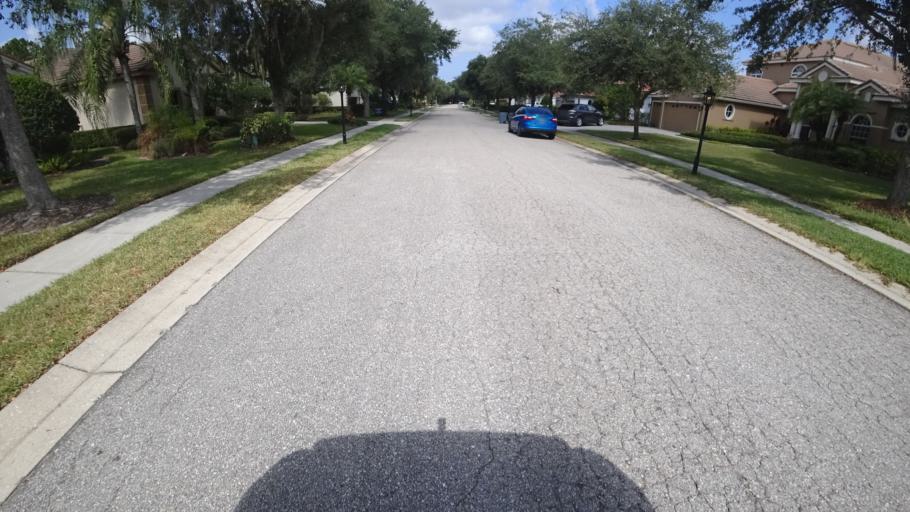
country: US
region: Florida
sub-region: Sarasota County
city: The Meadows
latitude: 27.3997
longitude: -82.4447
